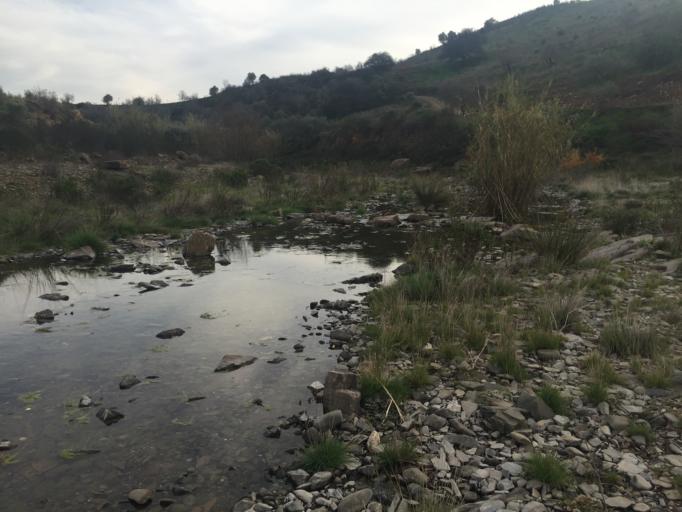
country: PT
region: Faro
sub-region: Castro Marim
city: Castro Marim
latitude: 37.2961
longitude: -7.6012
